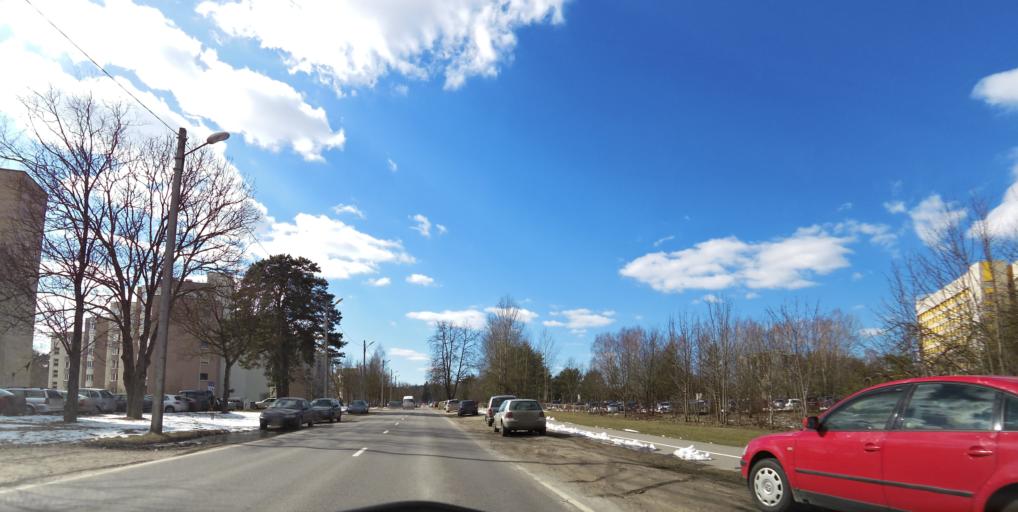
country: LT
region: Vilnius County
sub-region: Vilnius
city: Fabijoniskes
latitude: 54.7510
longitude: 25.2852
